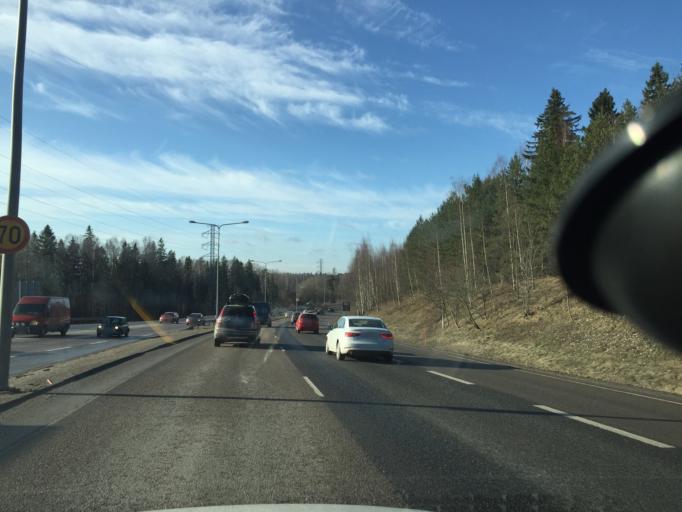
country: FI
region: Uusimaa
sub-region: Helsinki
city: Otaniemi
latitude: 60.2038
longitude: 24.8148
